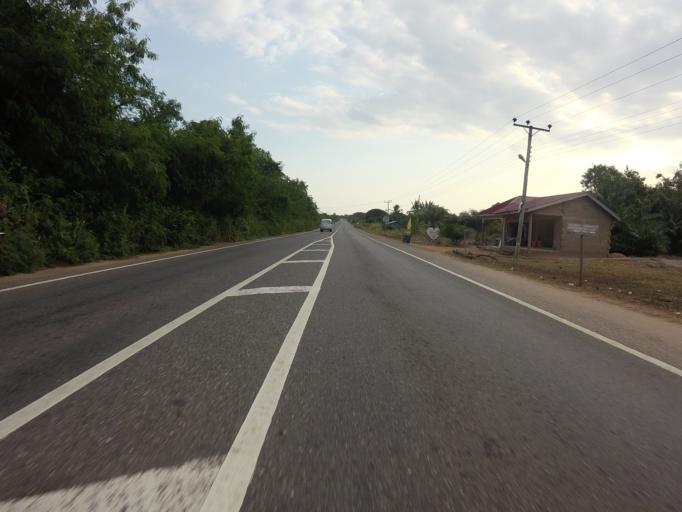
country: GH
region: Volta
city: Anloga
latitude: 6.1017
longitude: 0.5121
